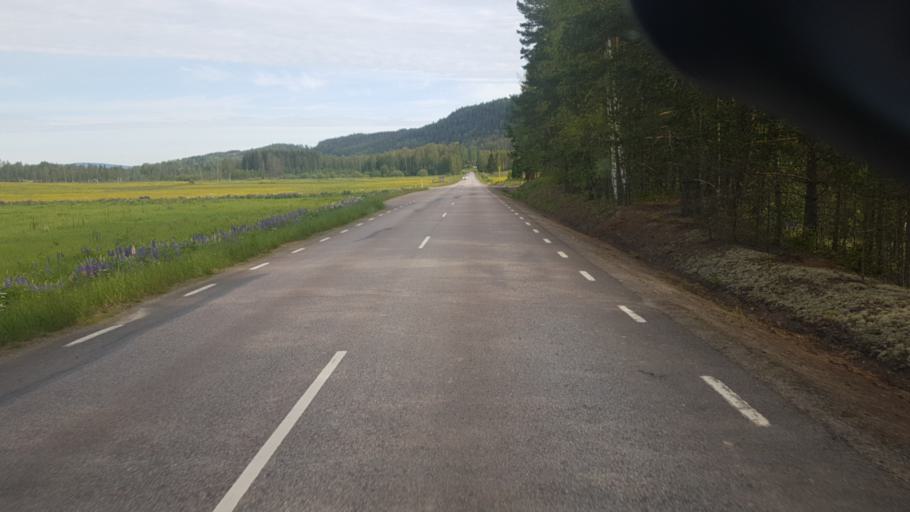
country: SE
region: Vaermland
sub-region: Arvika Kommun
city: Arvika
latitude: 59.7413
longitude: 12.6403
